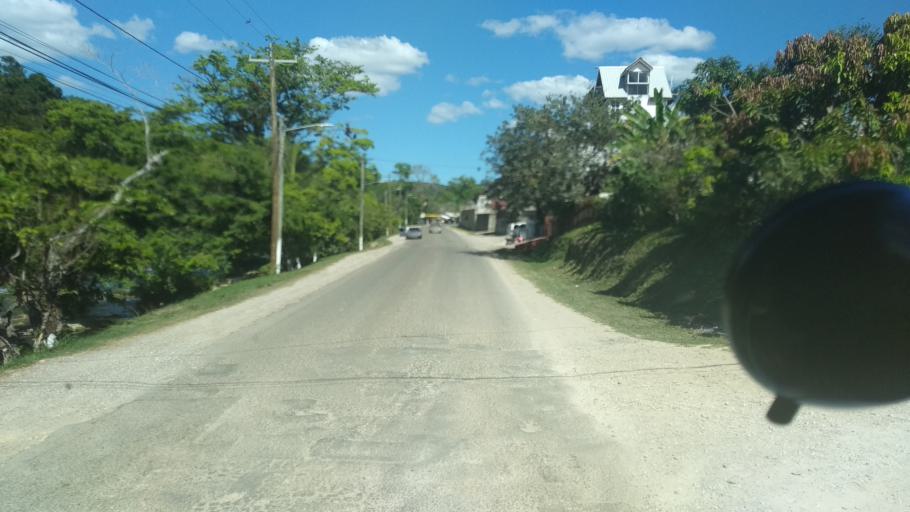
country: BZ
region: Cayo
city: Benque Viejo del Carmen
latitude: 17.0865
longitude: -89.1312
